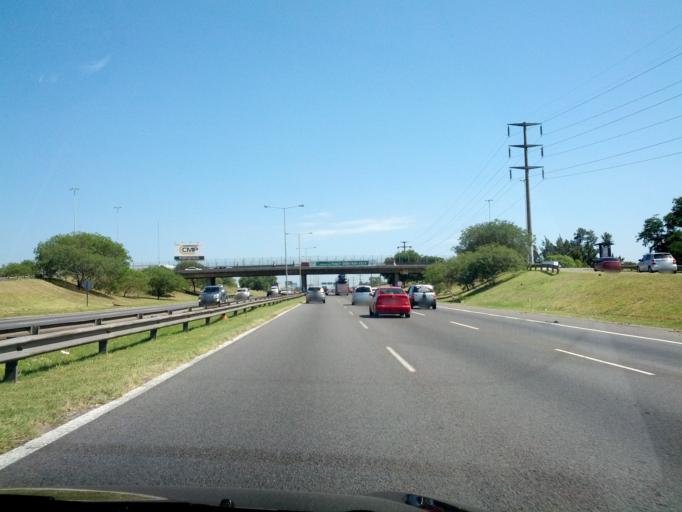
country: AR
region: Buenos Aires
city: Santa Catalina - Dique Lujan
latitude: -34.4178
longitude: -58.7224
